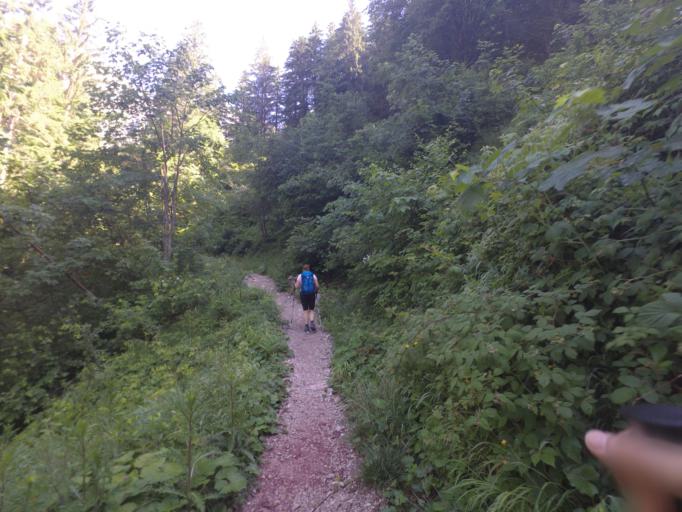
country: AT
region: Salzburg
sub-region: Politischer Bezirk Zell am See
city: Leogang
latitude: 47.4584
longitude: 12.7506
